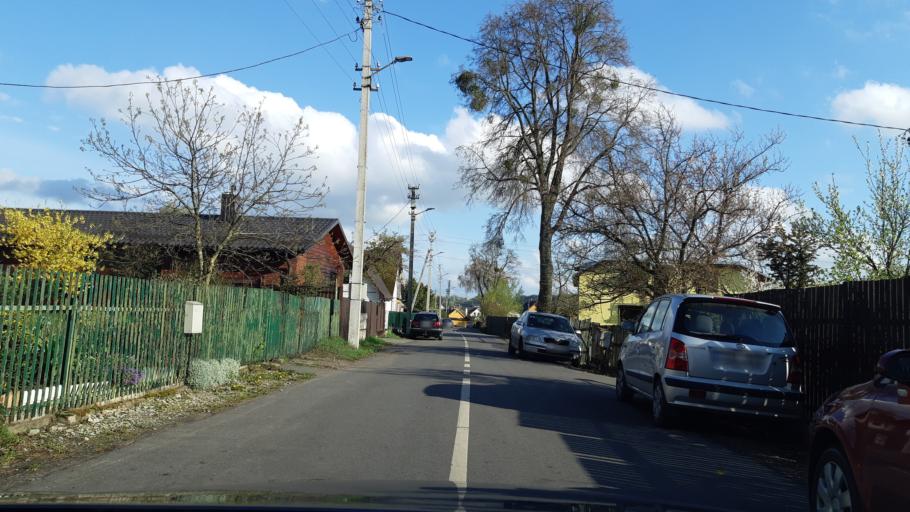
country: LT
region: Kauno apskritis
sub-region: Kaunas
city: Aleksotas
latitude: 54.8658
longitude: 23.9328
